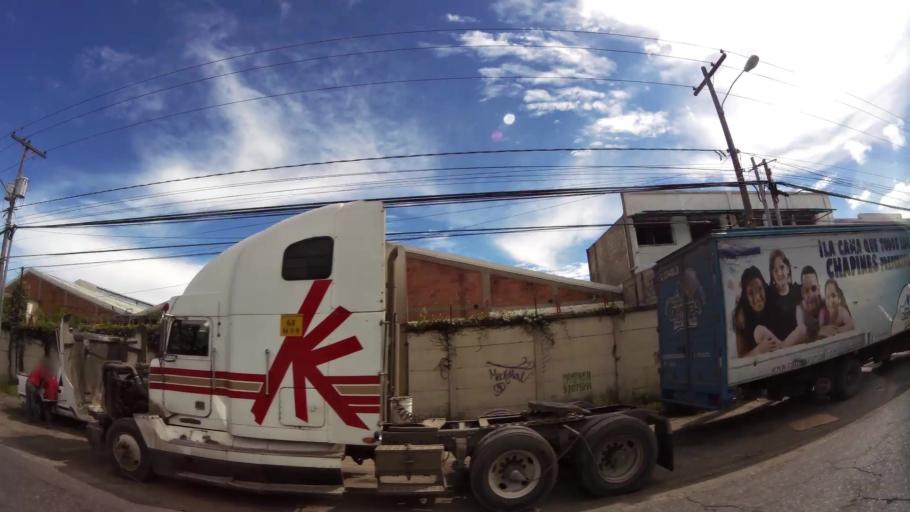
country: GT
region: Guatemala
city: Mixco
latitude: 14.6402
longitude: -90.5845
